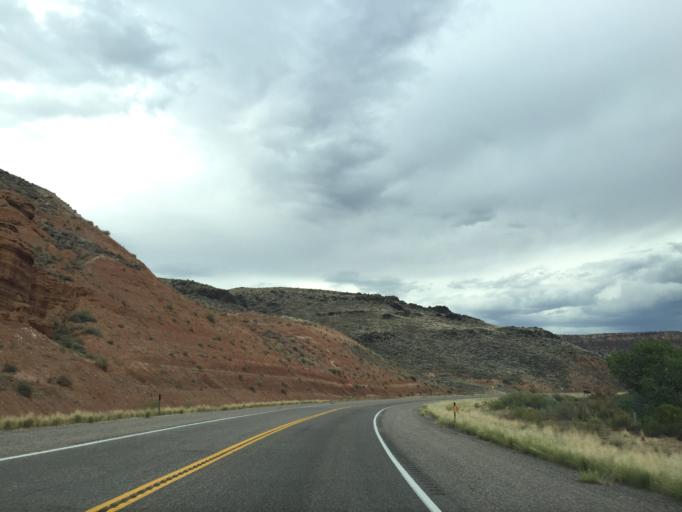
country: US
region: Utah
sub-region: Washington County
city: LaVerkin
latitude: 37.1784
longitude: -113.1174
